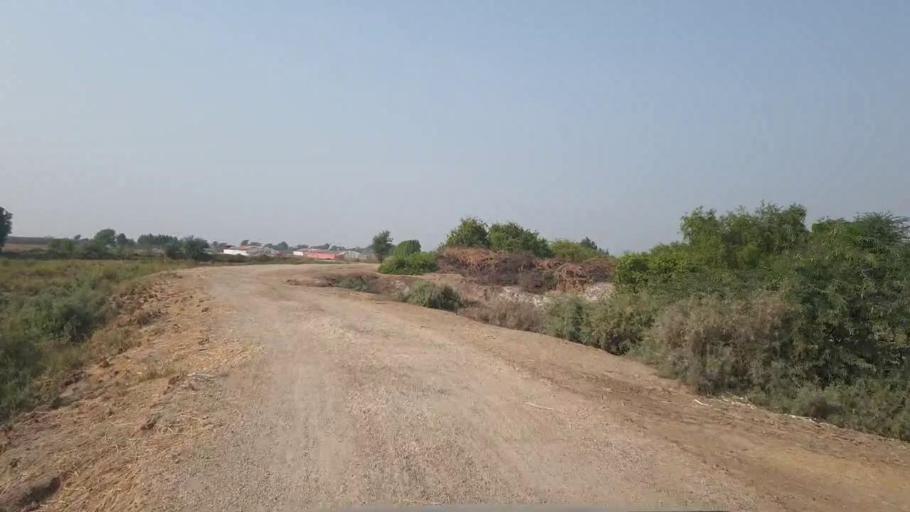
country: PK
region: Sindh
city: Tando Muhammad Khan
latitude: 25.0477
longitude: 68.3729
